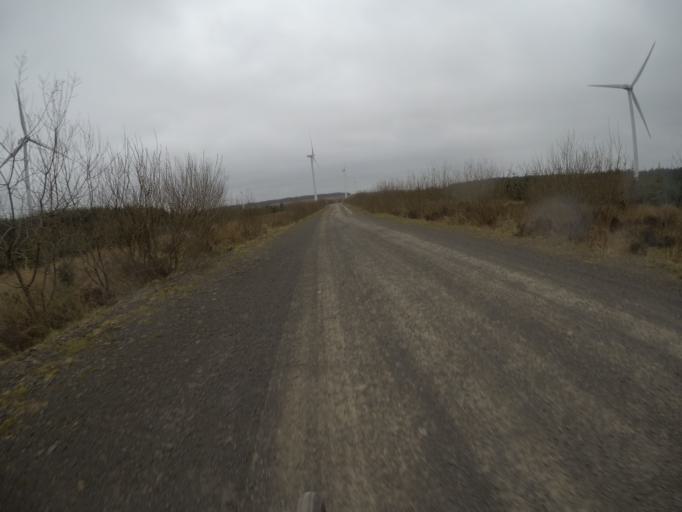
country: GB
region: Scotland
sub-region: East Ayrshire
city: Newmilns
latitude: 55.6533
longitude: -4.3247
